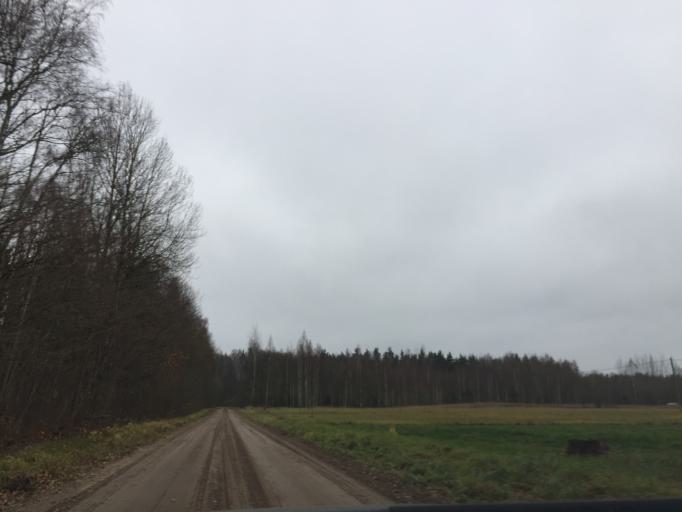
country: LV
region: Limbazu Rajons
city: Limbazi
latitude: 57.5075
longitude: 24.7594
